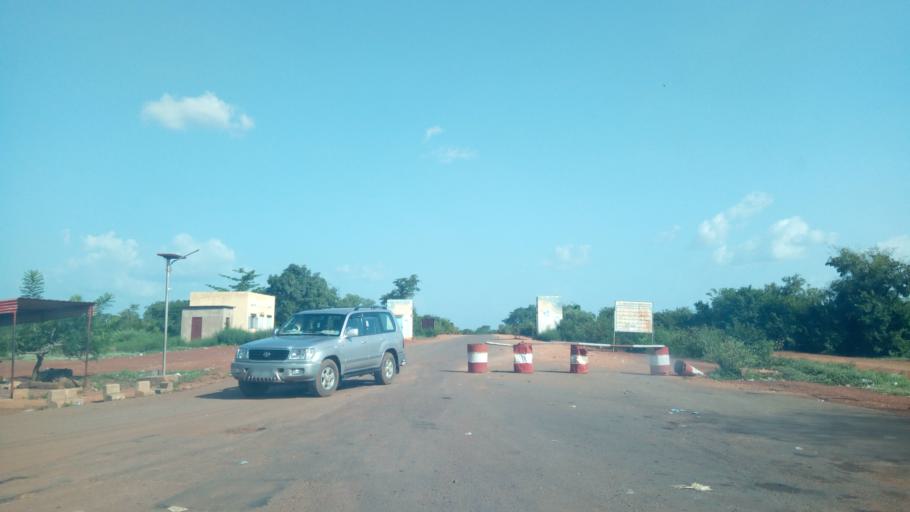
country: ML
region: Sikasso
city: Yorosso
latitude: 12.1885
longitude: -4.8422
